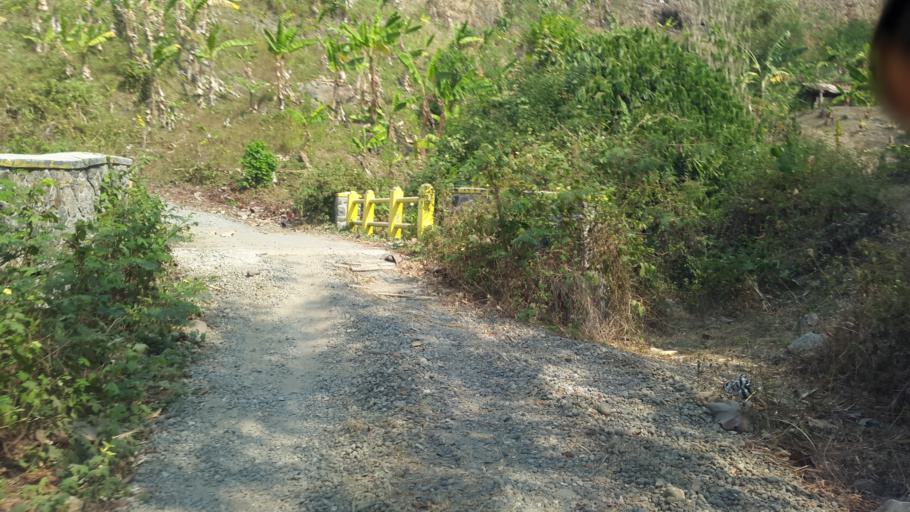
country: ID
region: West Java
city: Citarik
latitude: -7.0191
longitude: 106.5821
